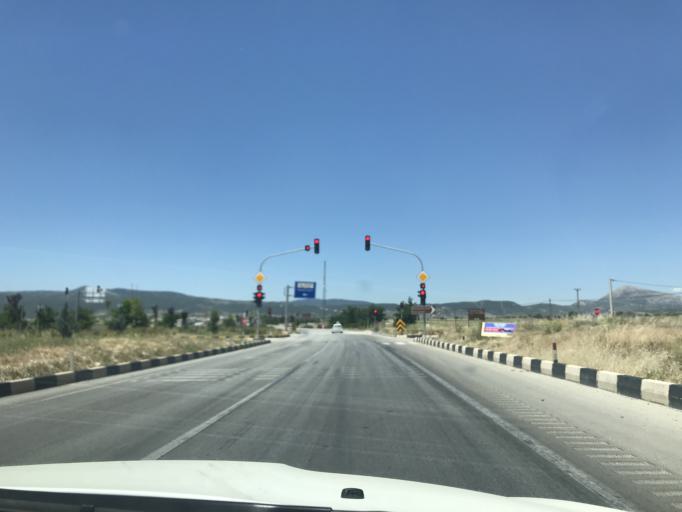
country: TR
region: Isparta
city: Keciborlu
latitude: 37.8974
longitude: 30.3855
